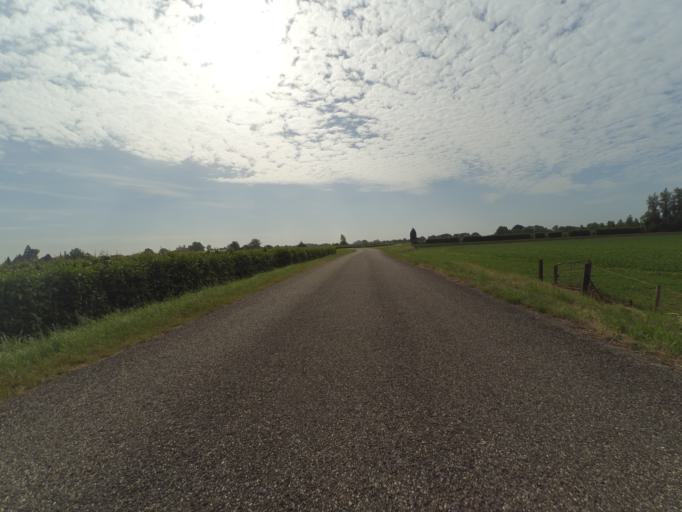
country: NL
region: Gelderland
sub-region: Gemeente Geldermalsen
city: Geldermalsen
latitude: 51.8899
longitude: 5.2512
